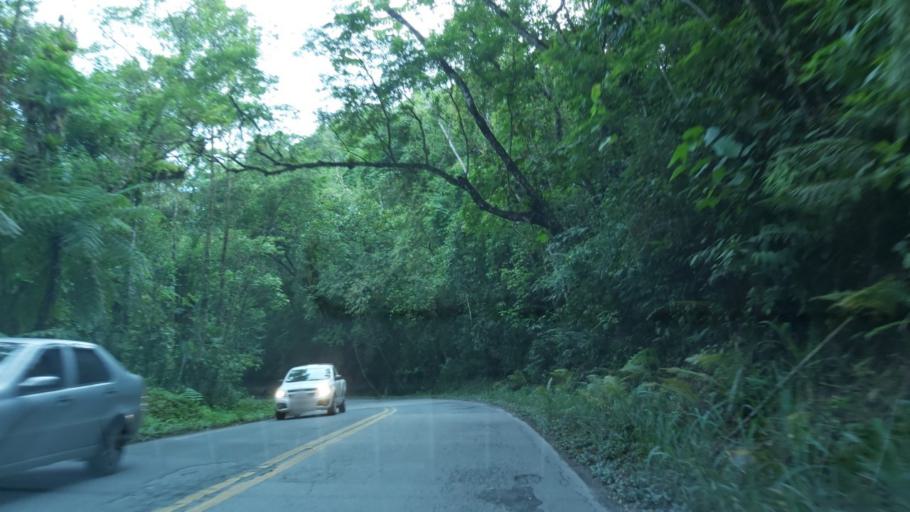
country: BR
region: Sao Paulo
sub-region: Juquia
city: Juquia
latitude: -24.0771
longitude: -47.6046
